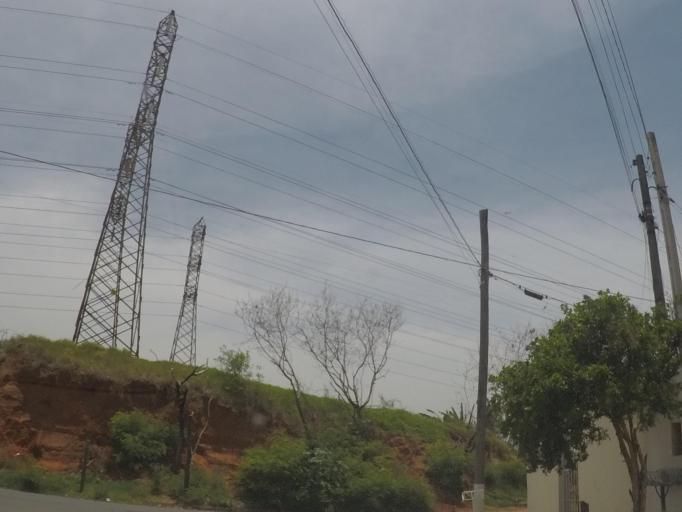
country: BR
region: Sao Paulo
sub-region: Hortolandia
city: Hortolandia
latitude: -22.8455
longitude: -47.1965
